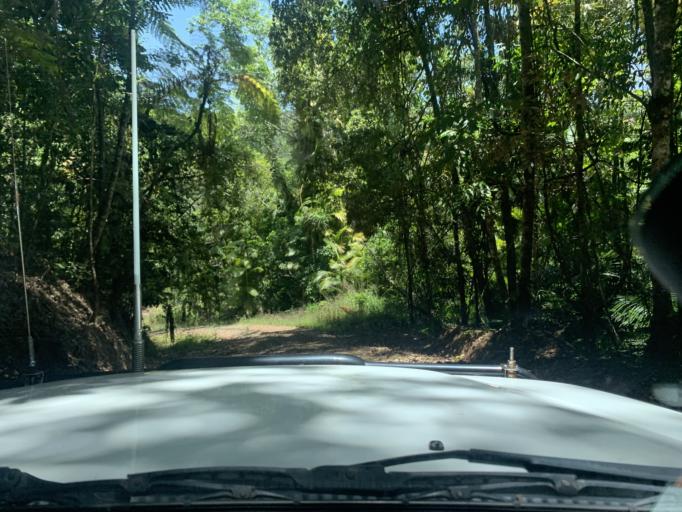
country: AU
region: Queensland
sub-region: Cairns
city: Woree
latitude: -16.9759
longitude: 145.6517
